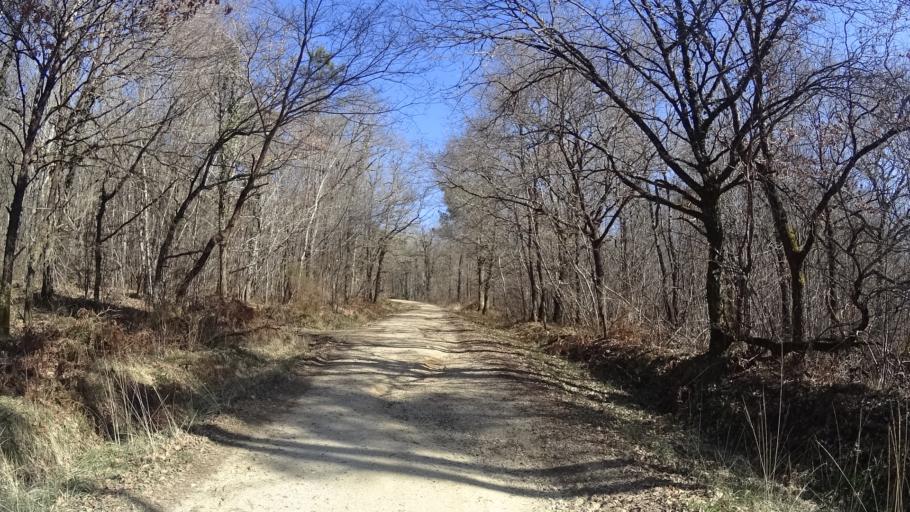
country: FR
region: Aquitaine
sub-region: Departement de la Dordogne
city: Montpon-Menesterol
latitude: 45.0953
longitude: 0.1912
